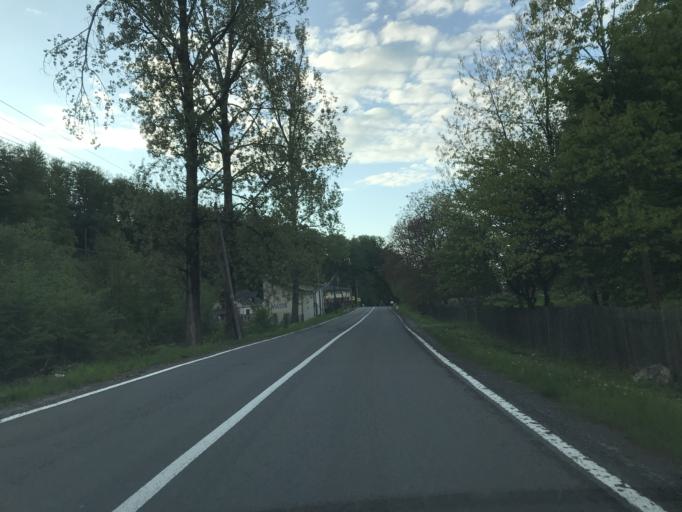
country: RO
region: Sibiu
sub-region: Comuna Cartisoara
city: Cartisoara
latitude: 45.6834
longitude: 24.5753
